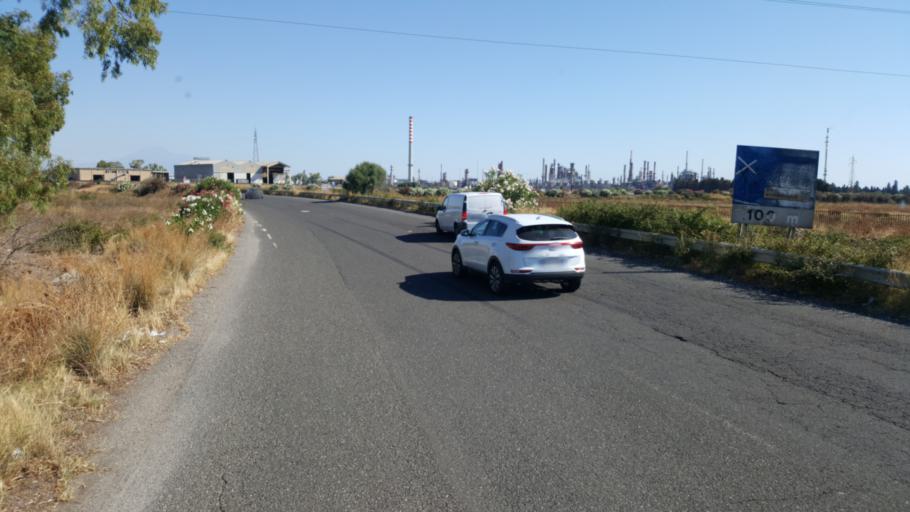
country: IT
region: Sicily
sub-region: Provincia di Siracusa
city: Melilli
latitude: 37.2000
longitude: 15.1639
